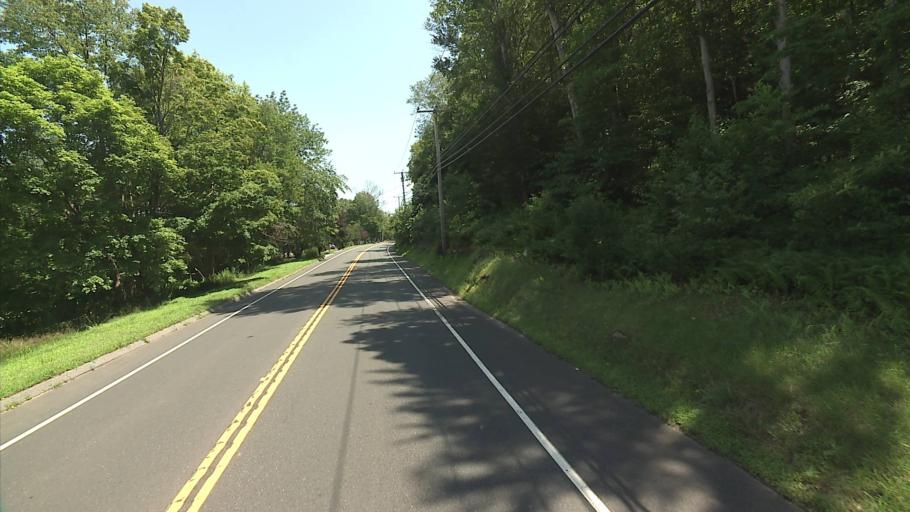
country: US
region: Connecticut
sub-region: Middlesex County
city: East Haddam
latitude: 41.4684
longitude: -72.4858
